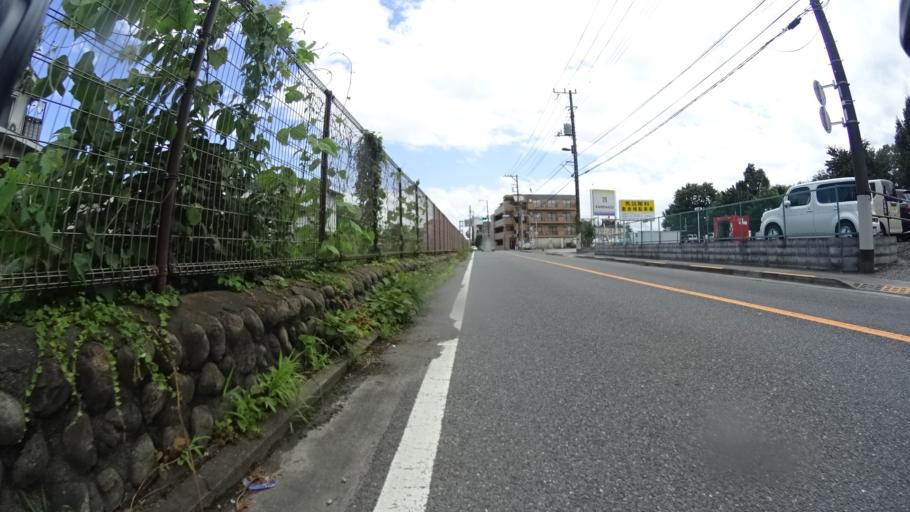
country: JP
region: Tokyo
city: Fussa
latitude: 35.7350
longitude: 139.3270
